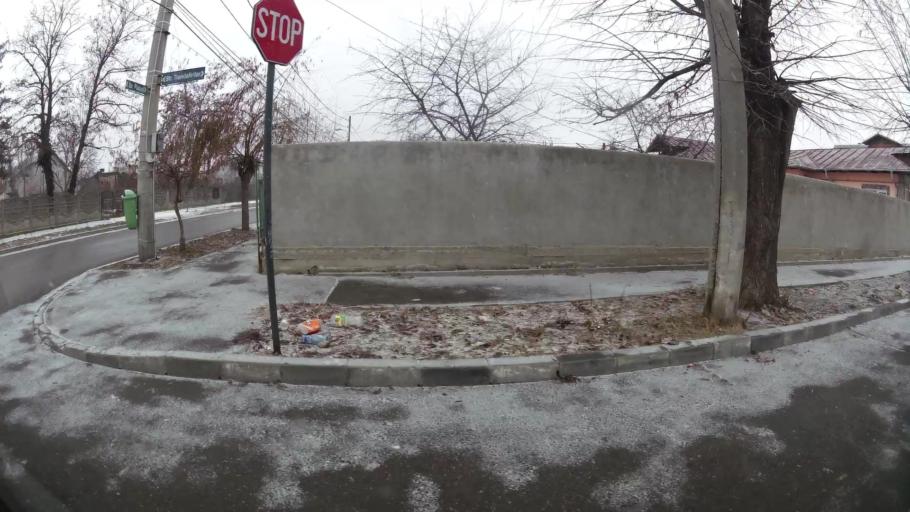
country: RO
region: Prahova
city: Ploiesti
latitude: 44.9487
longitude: 26.0496
